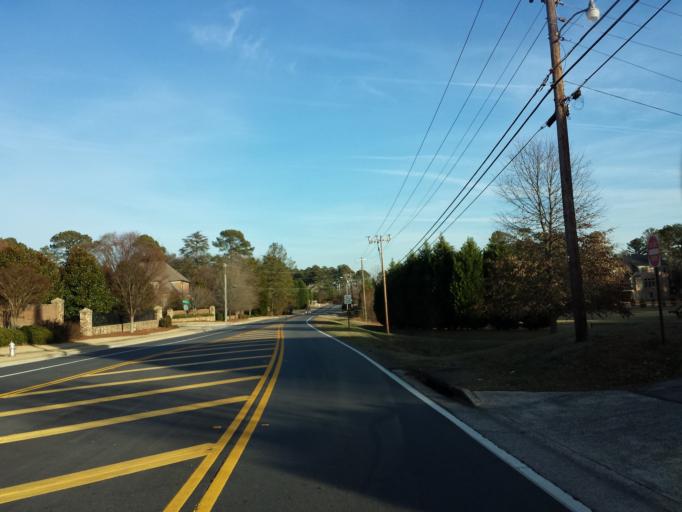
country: US
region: Georgia
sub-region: Cobb County
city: Marietta
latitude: 33.9831
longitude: -84.4767
